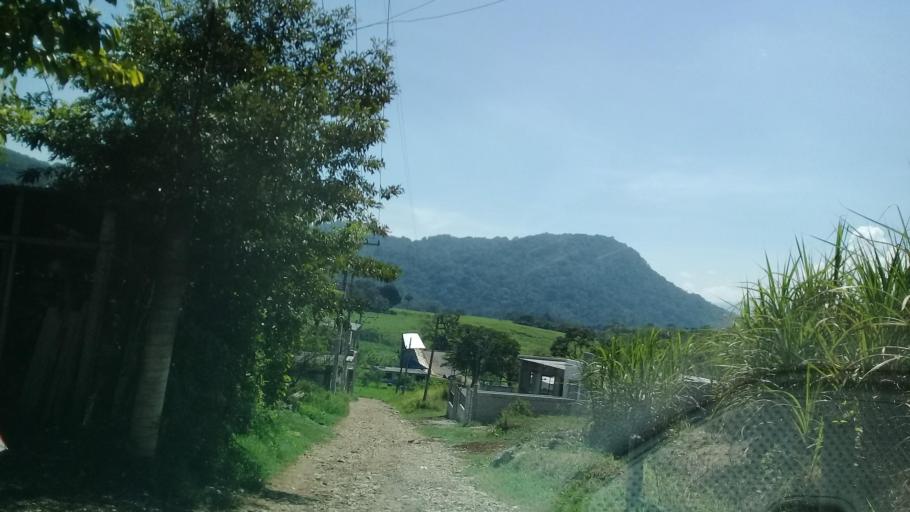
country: MX
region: Veracruz
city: Amatlan de los Reyes
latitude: 18.8446
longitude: -96.9116
